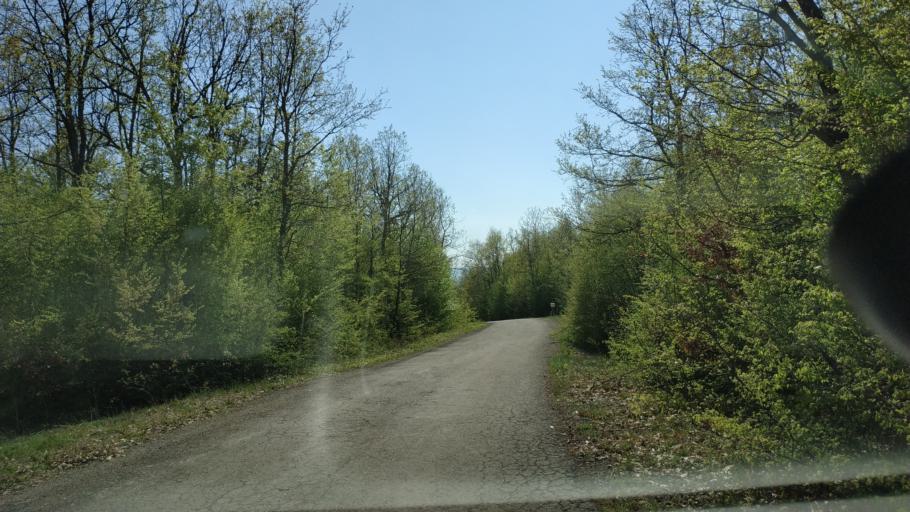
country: RS
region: Central Serbia
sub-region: Zajecarski Okrug
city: Soko Banja
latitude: 43.5035
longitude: 21.8897
